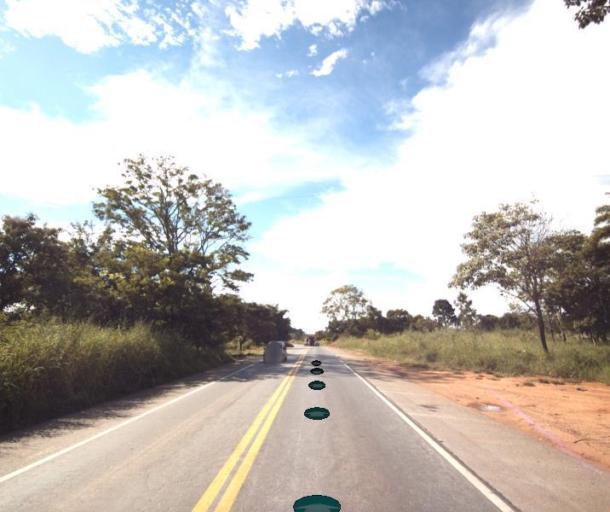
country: BR
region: Goias
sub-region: Jaragua
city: Jaragua
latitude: -15.5668
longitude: -49.4202
